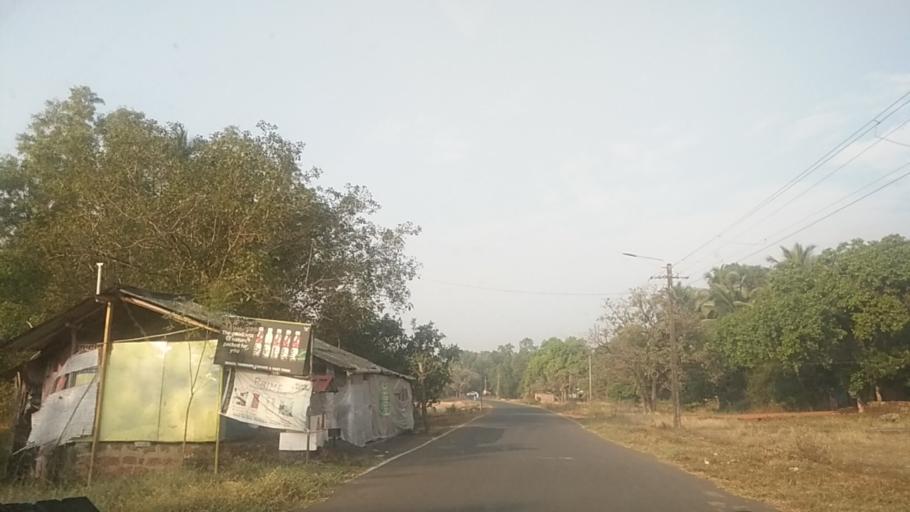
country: IN
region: Goa
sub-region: South Goa
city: Chinchinim
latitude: 15.2374
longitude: 73.9786
